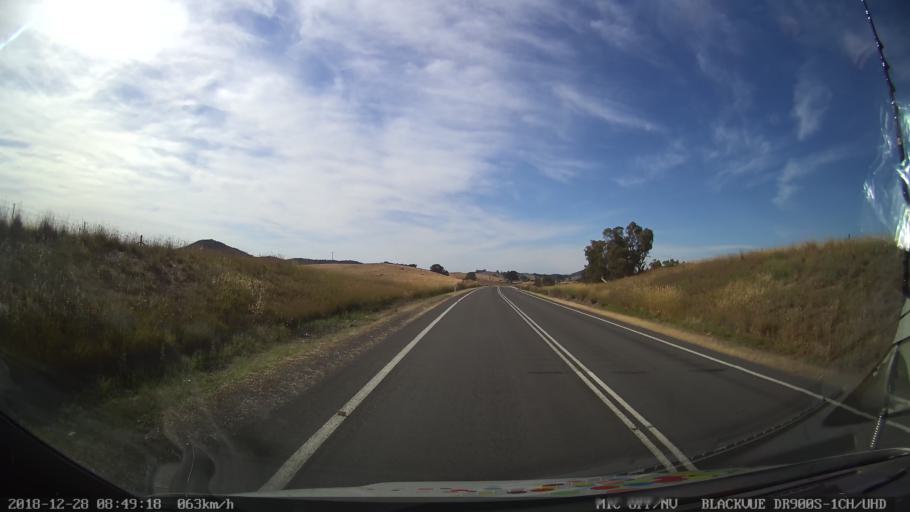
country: AU
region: New South Wales
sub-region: Upper Lachlan Shire
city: Crookwell
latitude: -34.0443
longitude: 149.3366
